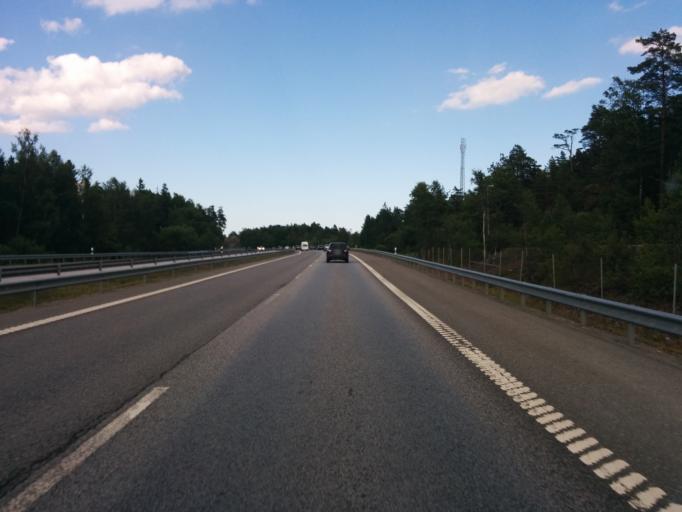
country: SE
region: Stockholm
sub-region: Nacka Kommun
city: Boo
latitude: 59.3223
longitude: 18.2923
